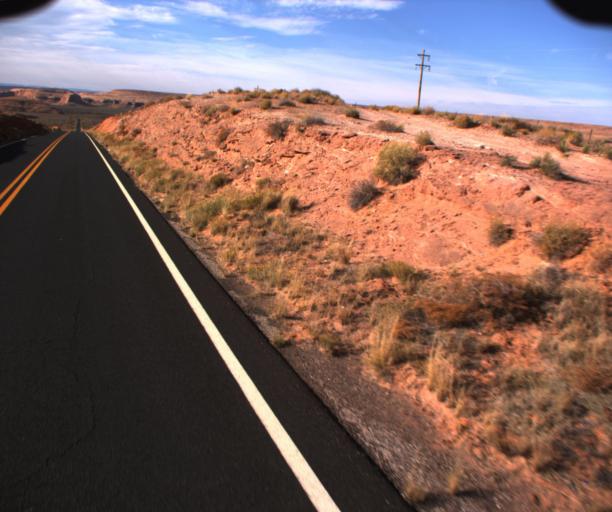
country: US
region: Arizona
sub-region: Apache County
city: Many Farms
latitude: 36.7894
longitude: -109.6525
